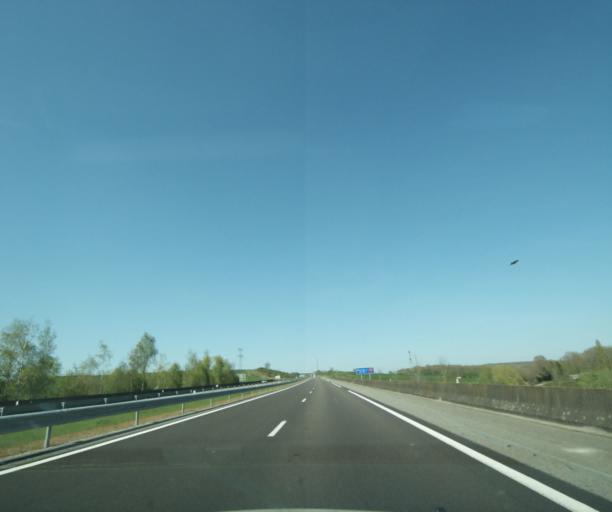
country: FR
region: Bourgogne
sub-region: Departement de la Nievre
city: Cosne-Cours-sur-Loire
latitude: 47.4511
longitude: 2.9481
